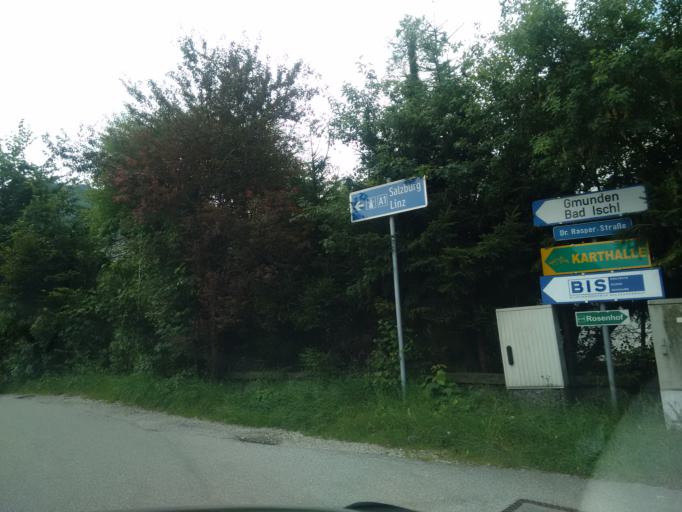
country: AT
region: Upper Austria
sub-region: Politischer Bezirk Gmunden
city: Ebensee
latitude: 47.8023
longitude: 13.7679
